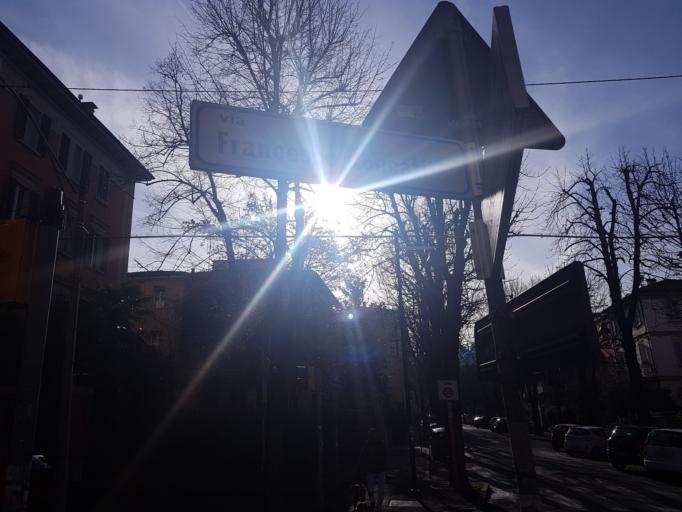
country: IT
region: Emilia-Romagna
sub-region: Provincia di Bologna
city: Bologna
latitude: 44.4934
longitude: 11.3252
